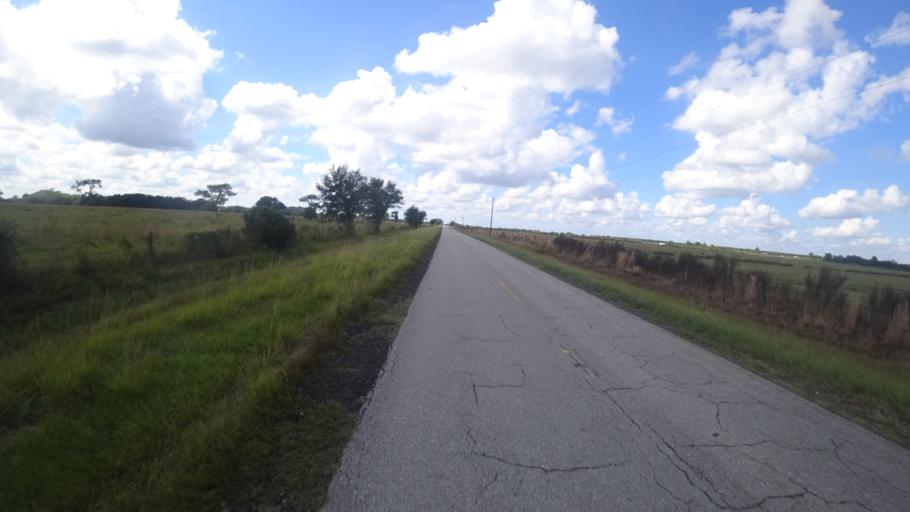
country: US
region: Florida
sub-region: Sarasota County
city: Warm Mineral Springs
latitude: 27.2737
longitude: -82.1638
